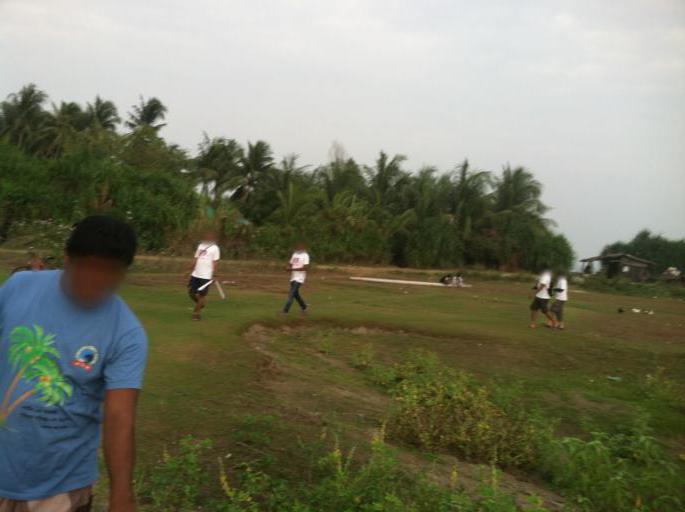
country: BD
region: Chittagong
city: Teknaf
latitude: 20.6187
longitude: 92.3251
